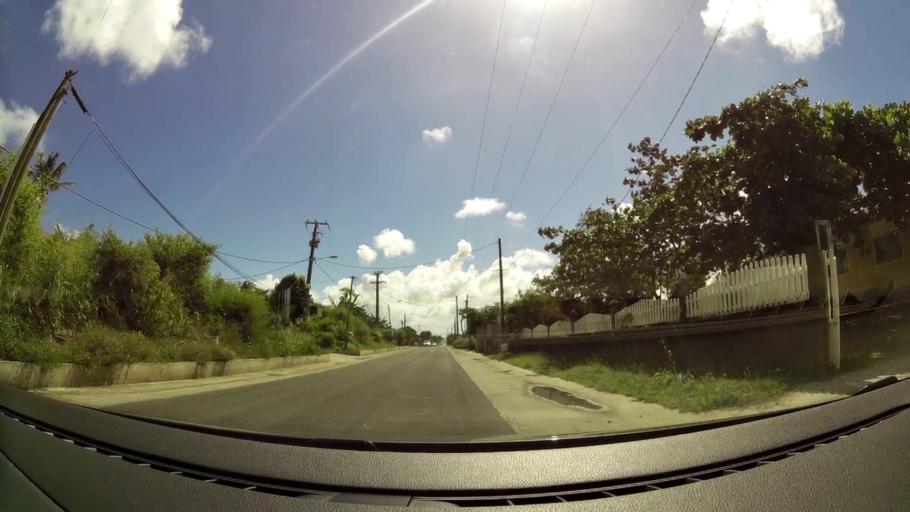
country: GP
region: Guadeloupe
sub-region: Guadeloupe
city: Petit-Canal
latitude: 16.4142
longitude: -61.4705
